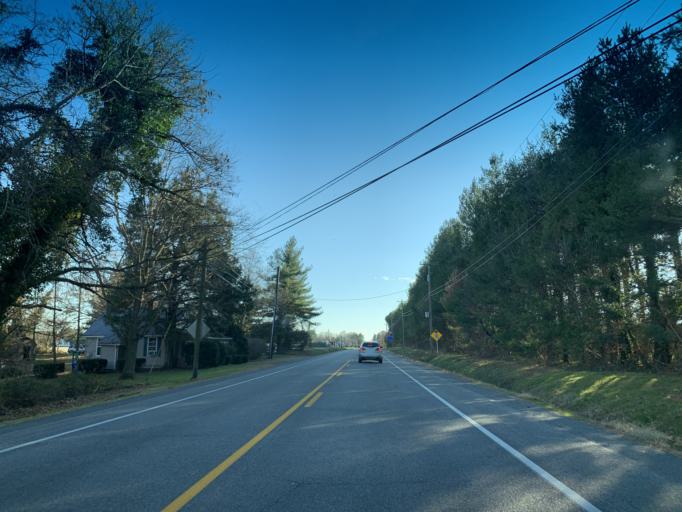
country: US
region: Delaware
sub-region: New Castle County
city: Middletown
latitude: 39.3532
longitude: -75.8774
